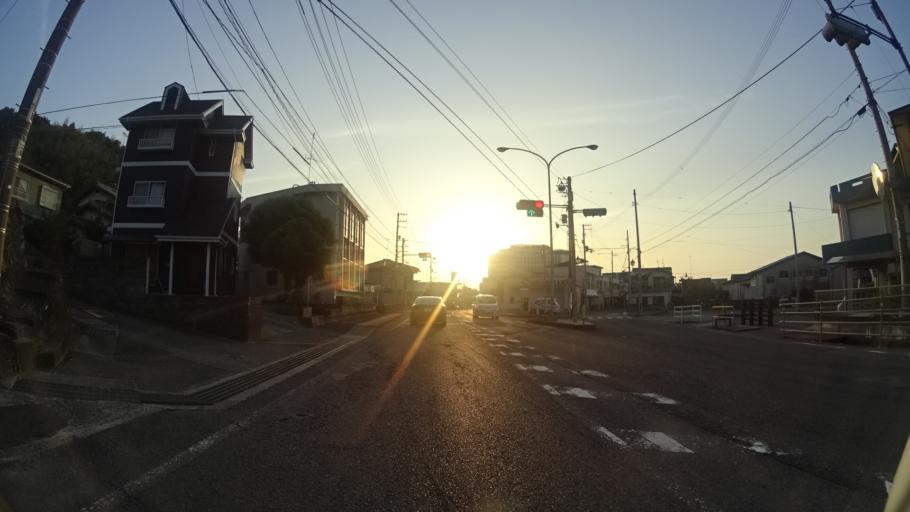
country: JP
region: Ehime
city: Kawanoecho
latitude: 33.9902
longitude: 133.5909
